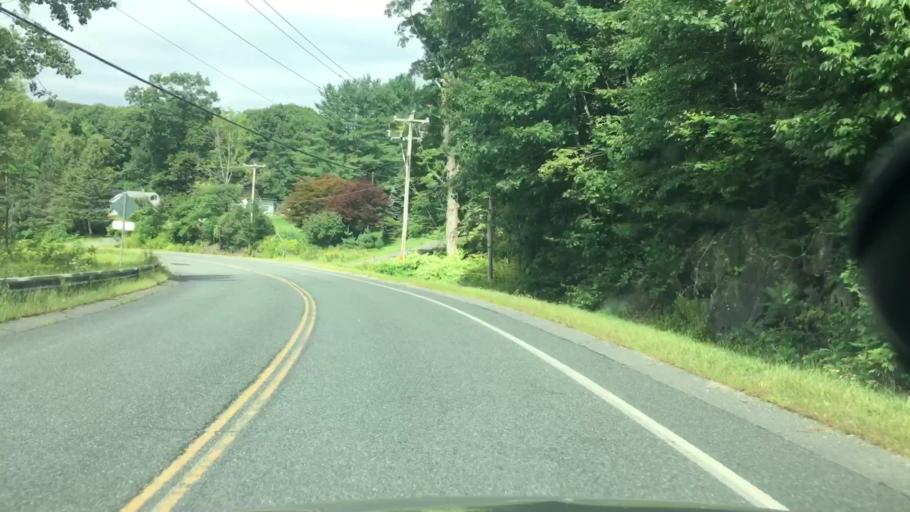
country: US
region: Massachusetts
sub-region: Franklin County
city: Colrain
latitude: 42.6688
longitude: -72.6852
